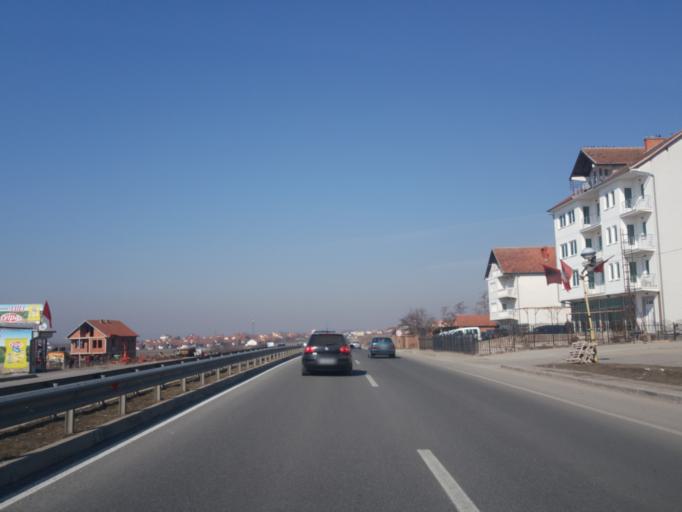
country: XK
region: Pristina
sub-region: Komuna e Obiliqit
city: Obiliq
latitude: 42.7539
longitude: 21.0378
